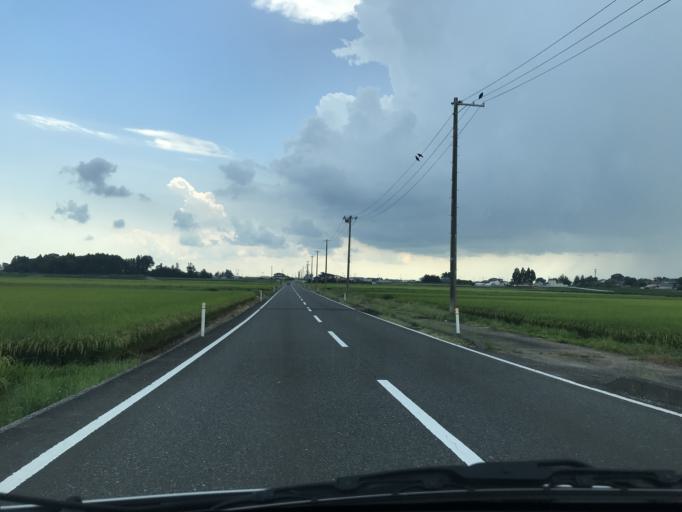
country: JP
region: Iwate
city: Ichinoseki
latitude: 38.7675
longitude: 141.0695
